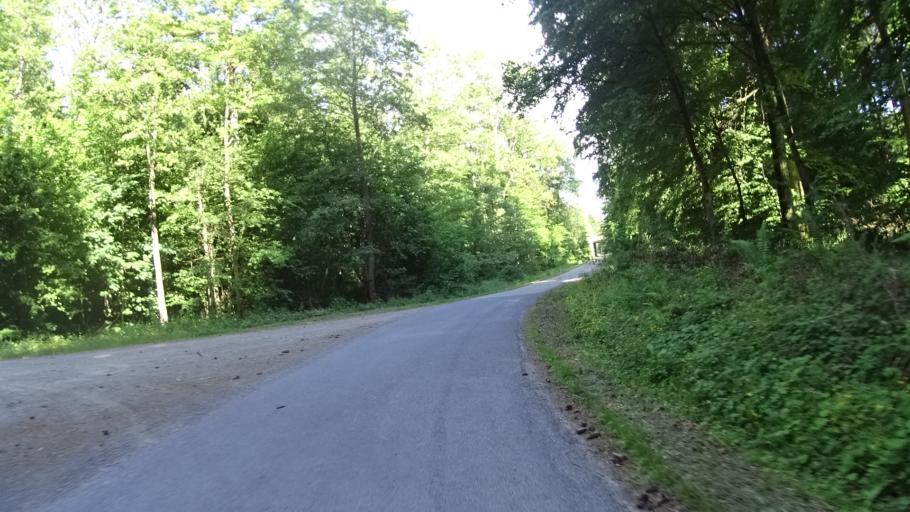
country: DE
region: Baden-Wuerttemberg
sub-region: Regierungsbezirk Stuttgart
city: Buch am Ahorn
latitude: 49.5318
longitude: 9.5741
